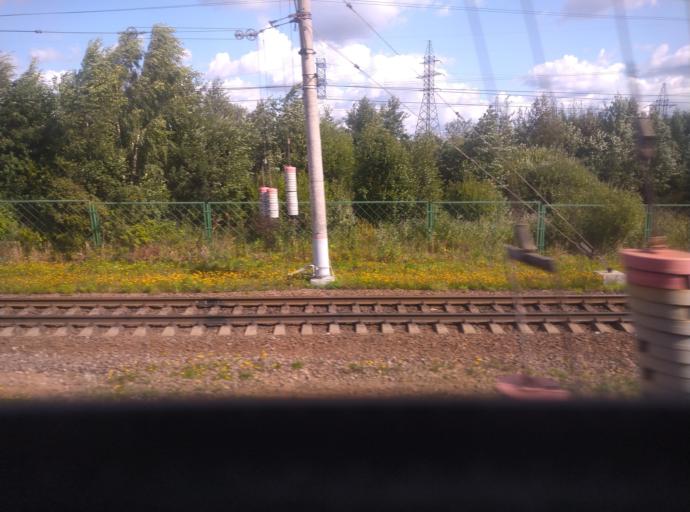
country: RU
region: St.-Petersburg
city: Kolpino
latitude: 59.7629
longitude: 30.5778
